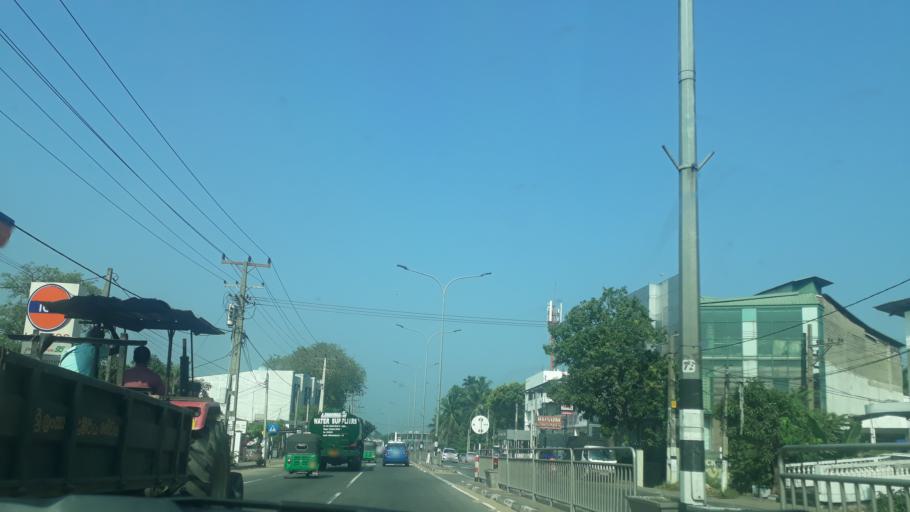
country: LK
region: Western
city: Wattala
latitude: 6.9678
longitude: 79.9045
